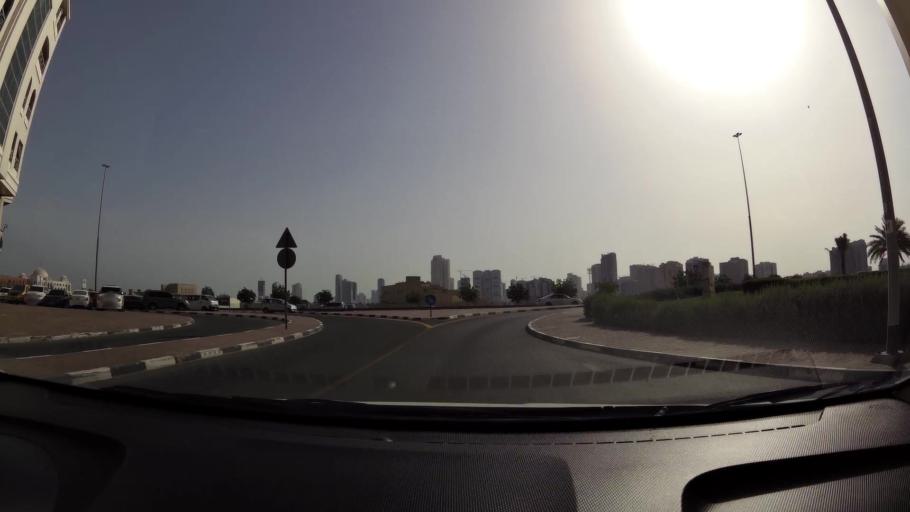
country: AE
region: Ash Shariqah
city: Sharjah
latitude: 25.2915
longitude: 55.3528
